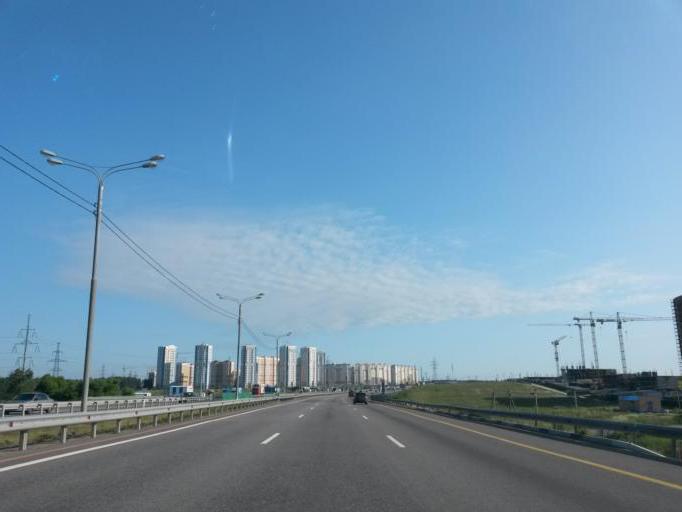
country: RU
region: Moskovskaya
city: Vostryakovo
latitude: 55.3849
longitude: 37.7764
